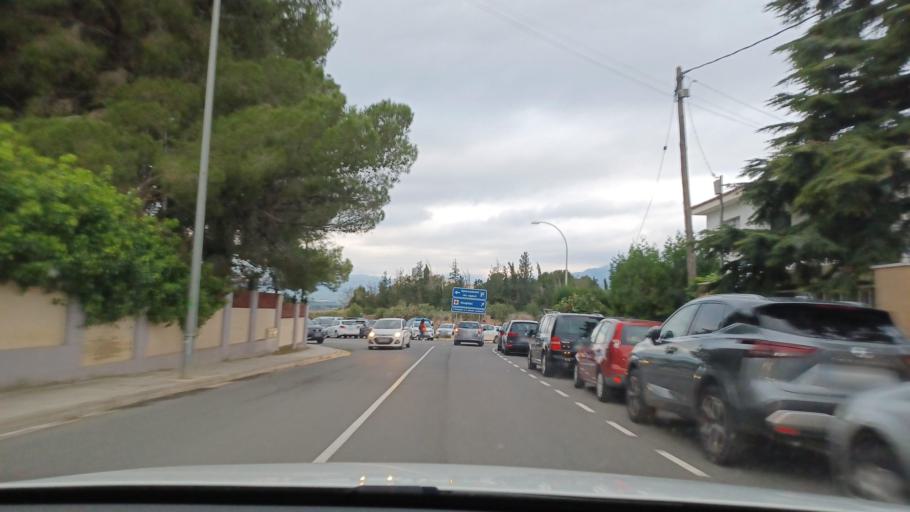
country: ES
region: Catalonia
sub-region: Provincia de Tarragona
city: Tortosa
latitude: 40.8120
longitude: 0.5275
